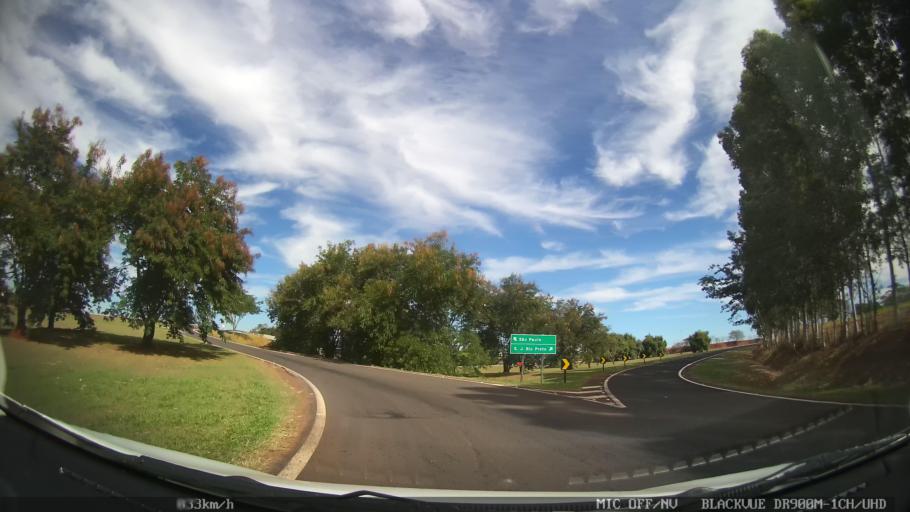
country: BR
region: Sao Paulo
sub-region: Taquaritinga
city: Taquaritinga
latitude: -21.4138
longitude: -48.6857
